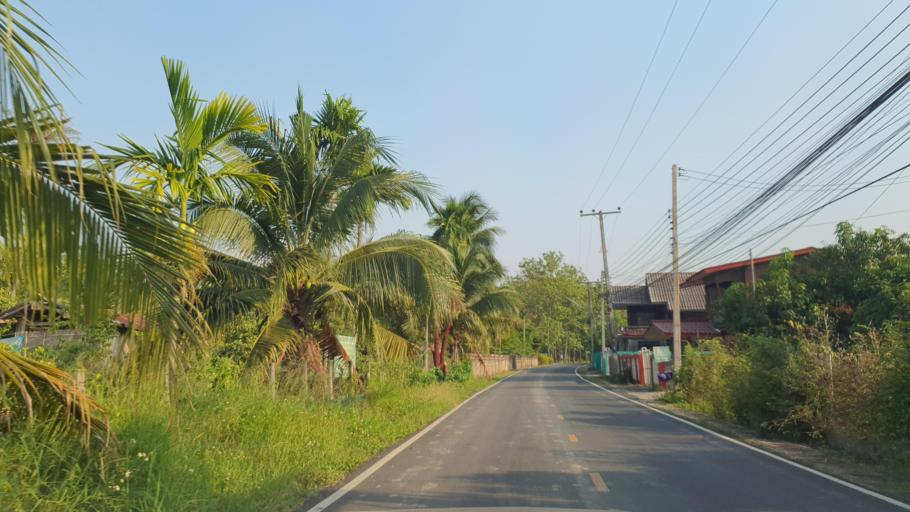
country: TH
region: Chiang Mai
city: Mae Wang
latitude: 18.6109
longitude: 98.8216
